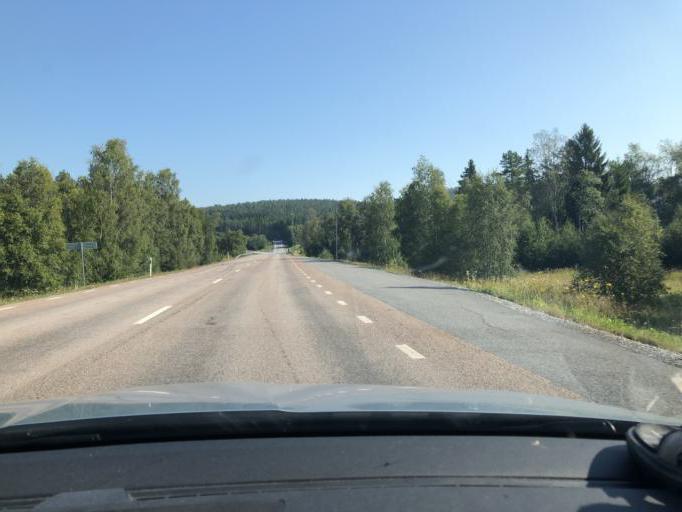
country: SE
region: Vaesternorrland
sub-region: Kramfors Kommun
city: Nordingra
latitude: 62.9314
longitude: 18.0873
